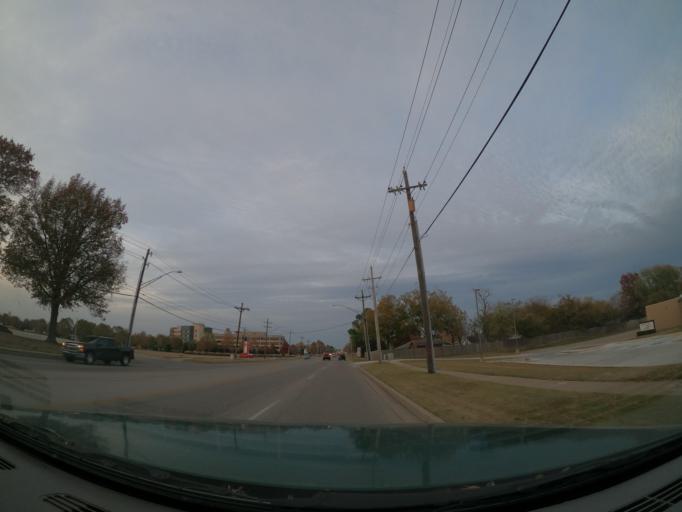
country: US
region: Oklahoma
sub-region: Tulsa County
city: Broken Arrow
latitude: 36.0206
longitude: -95.7974
